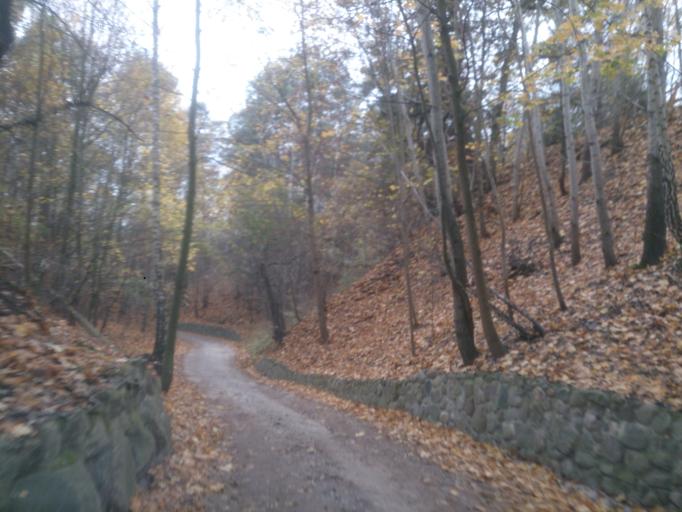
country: PL
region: Kujawsko-Pomorskie
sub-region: Powiat brodnicki
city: Brodnica
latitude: 53.3239
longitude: 19.3744
